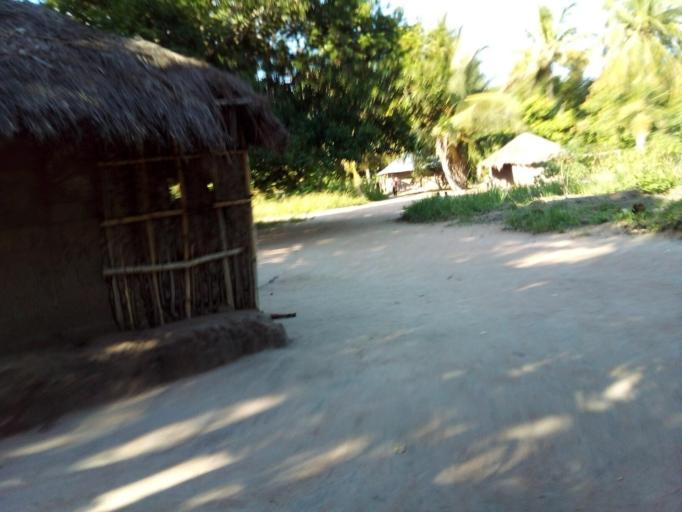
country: MZ
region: Zambezia
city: Quelimane
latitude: -17.5743
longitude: 36.8651
